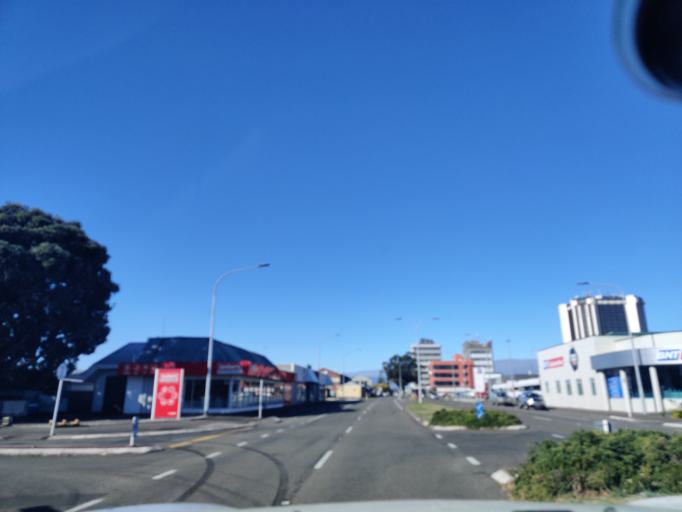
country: NZ
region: Manawatu-Wanganui
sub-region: Palmerston North City
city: Palmerston North
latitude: -40.3543
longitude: 175.6058
